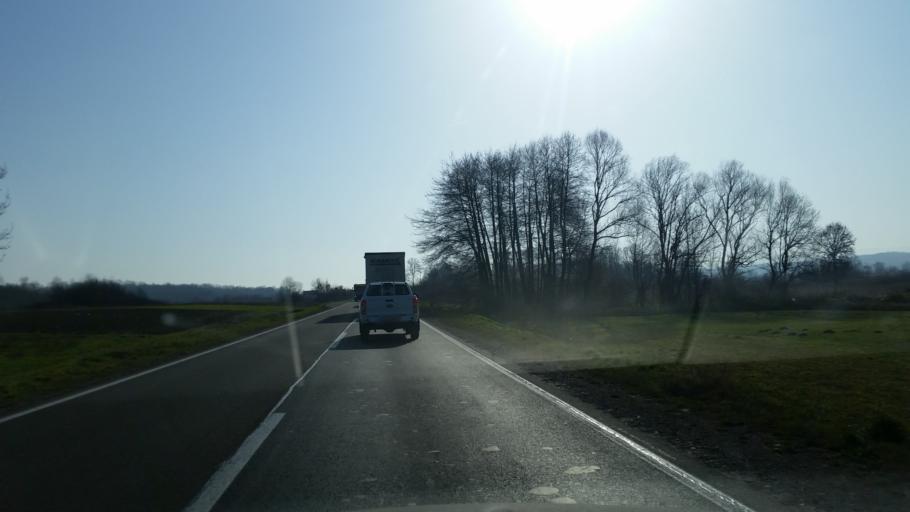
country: RS
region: Central Serbia
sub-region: Kolubarski Okrug
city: Lajkovac
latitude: 44.3305
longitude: 20.2184
